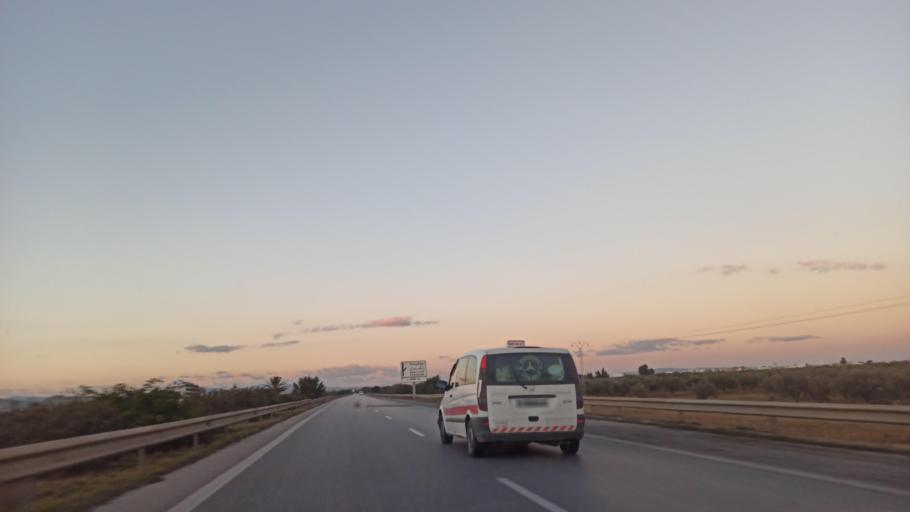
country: TN
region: Nabul
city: Al Hammamat
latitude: 36.2852
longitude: 10.4376
